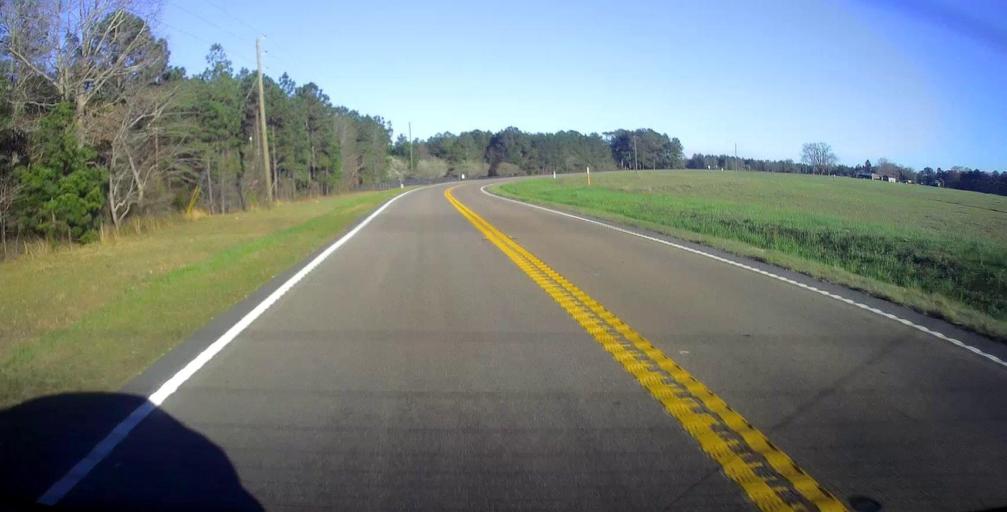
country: US
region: Georgia
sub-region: Taylor County
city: Butler
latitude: 32.4983
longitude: -84.4032
